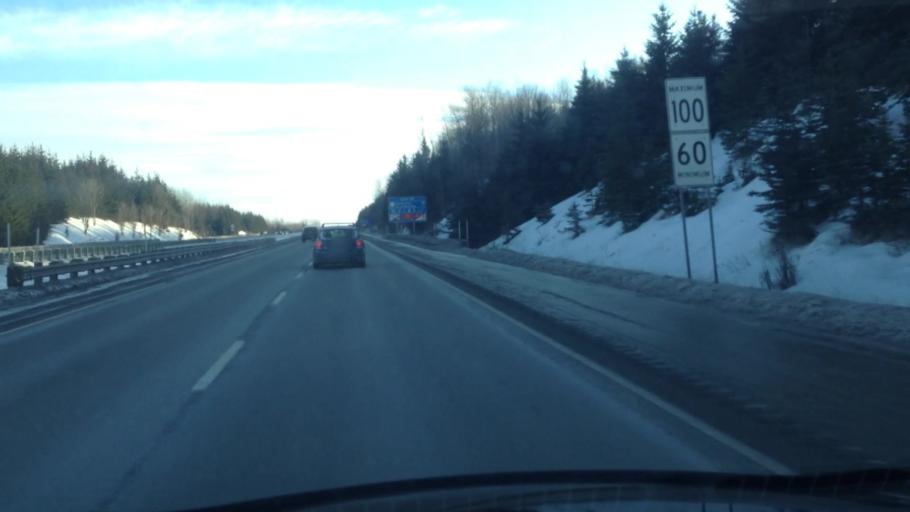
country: CA
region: Quebec
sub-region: Laurentides
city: Prevost
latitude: 45.8585
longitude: -74.0805
